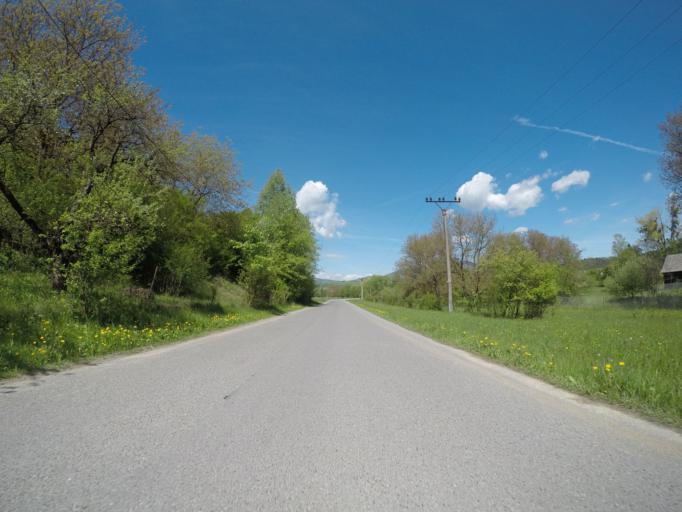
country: SK
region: Banskobystricky
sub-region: Okres Banska Bystrica
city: Banska Bystrica
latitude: 48.7332
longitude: 19.2032
